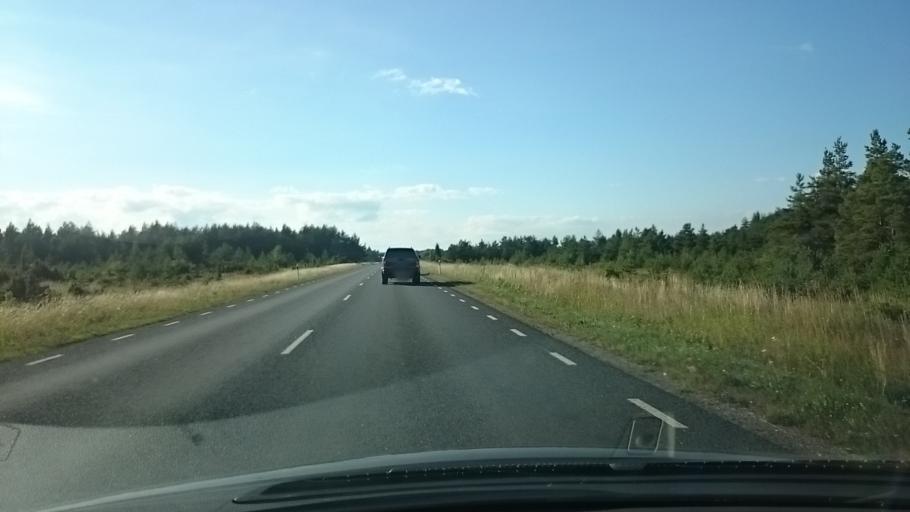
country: EE
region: Saare
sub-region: Orissaare vald
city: Orissaare
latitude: 58.5855
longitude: 23.3468
